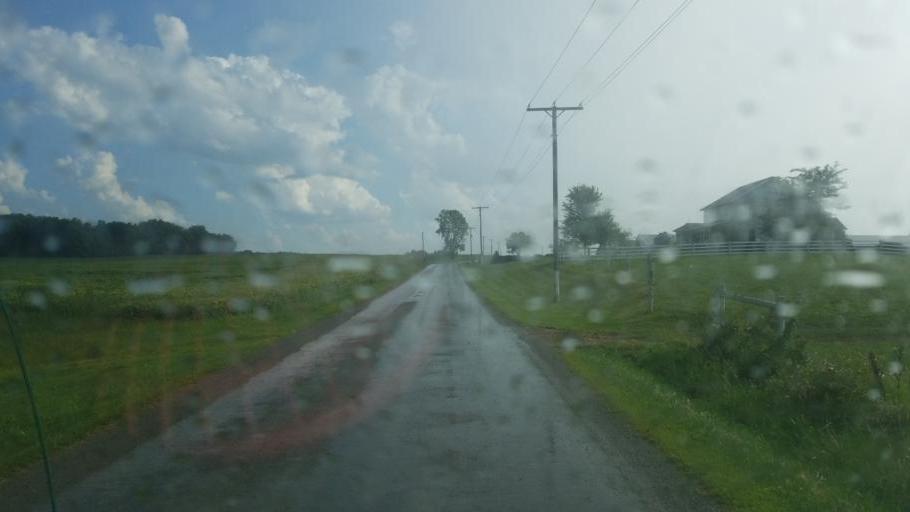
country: US
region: Ohio
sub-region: Huron County
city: Greenwich
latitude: 40.9842
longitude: -82.5579
